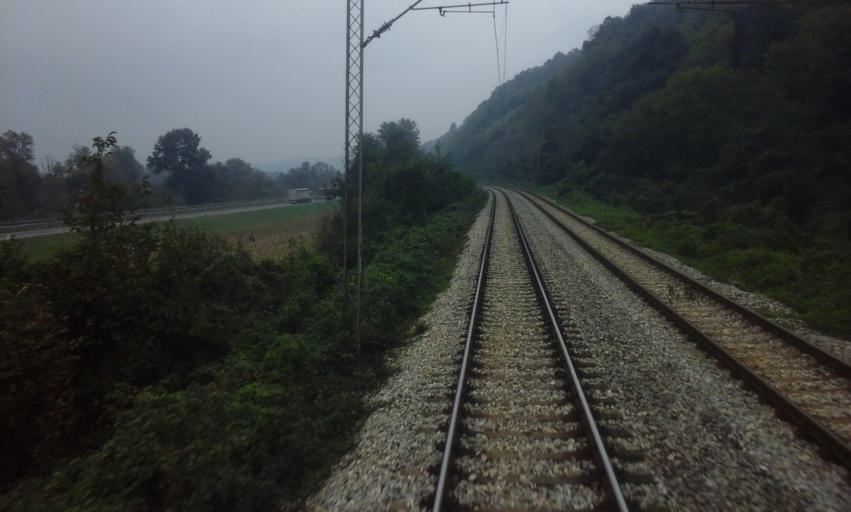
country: RS
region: Central Serbia
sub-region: Pomoravski Okrug
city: Jagodina
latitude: 44.0748
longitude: 21.1907
